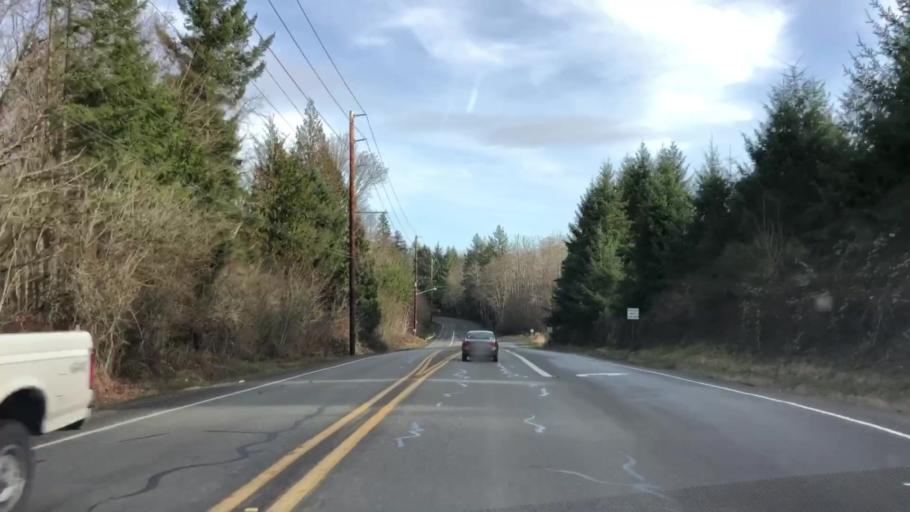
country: US
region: Washington
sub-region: Kitsap County
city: Indianola
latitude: 47.7846
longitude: -122.5474
